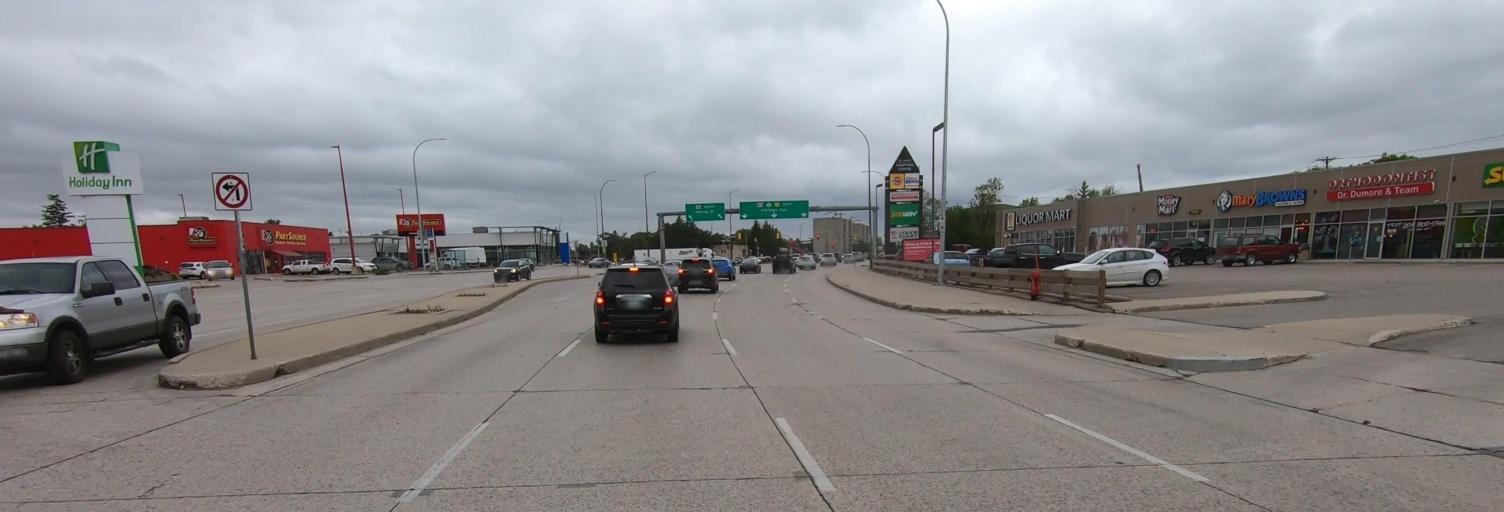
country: CA
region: Manitoba
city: Winnipeg
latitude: 49.8751
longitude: -97.2603
